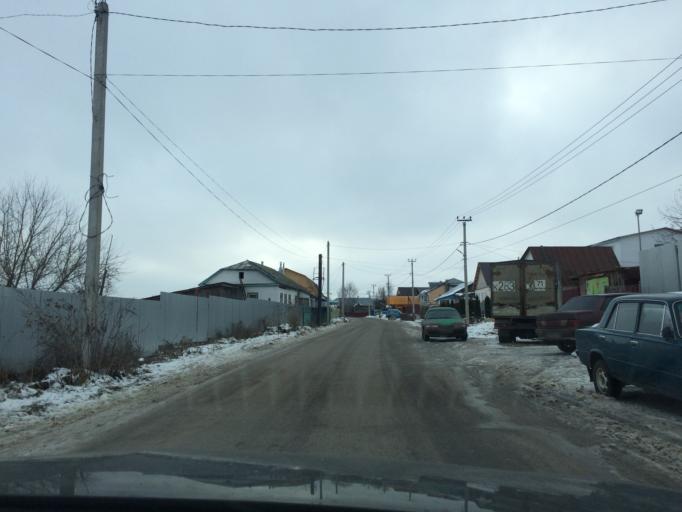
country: RU
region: Tula
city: Plavsk
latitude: 53.7082
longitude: 37.2979
